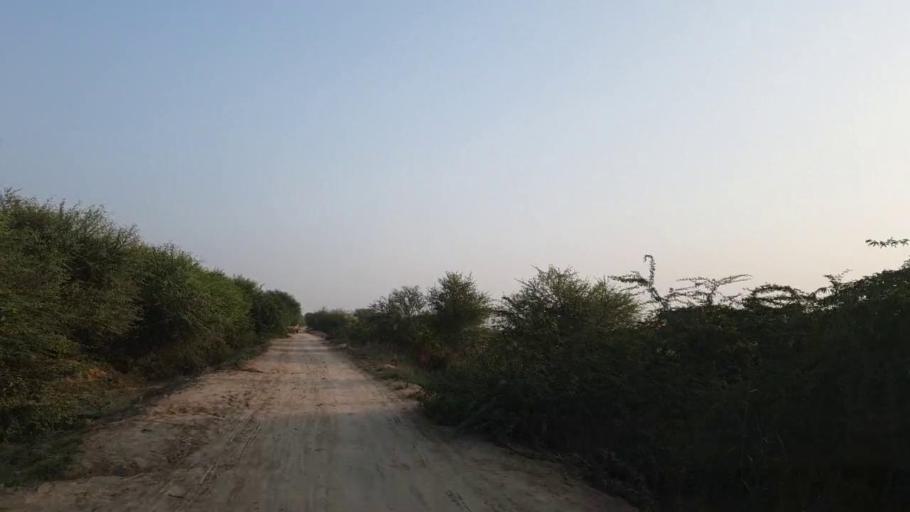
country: PK
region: Sindh
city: Kario
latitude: 24.8591
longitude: 68.6258
